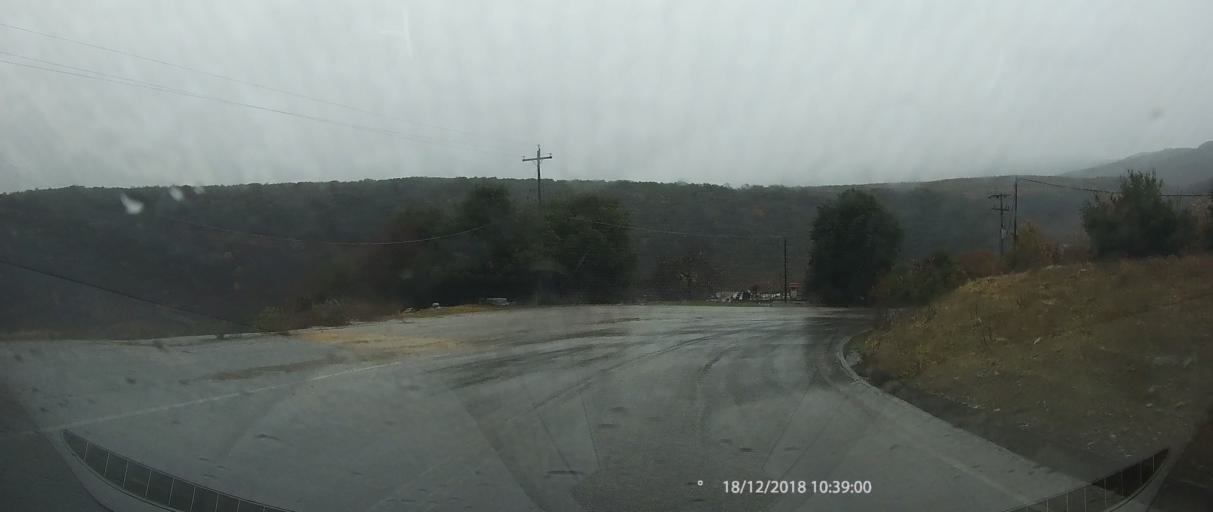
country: GR
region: Central Macedonia
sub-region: Nomos Pierias
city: Kato Milia
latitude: 40.2168
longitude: 22.3159
